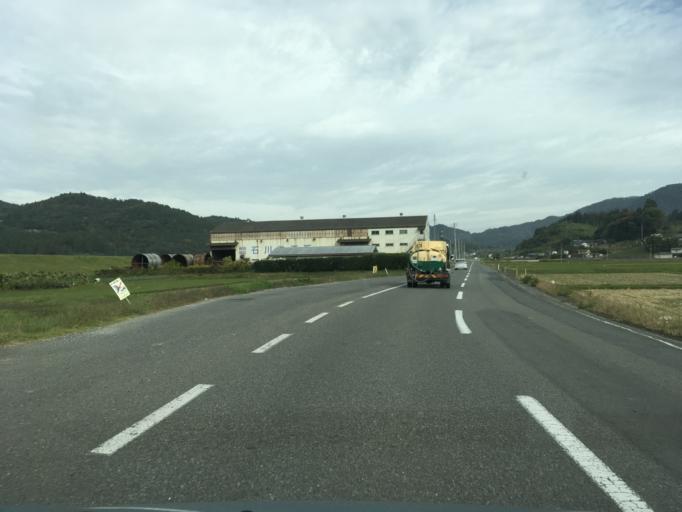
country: JP
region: Iwate
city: Ichinoseki
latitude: 38.9393
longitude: 141.2495
